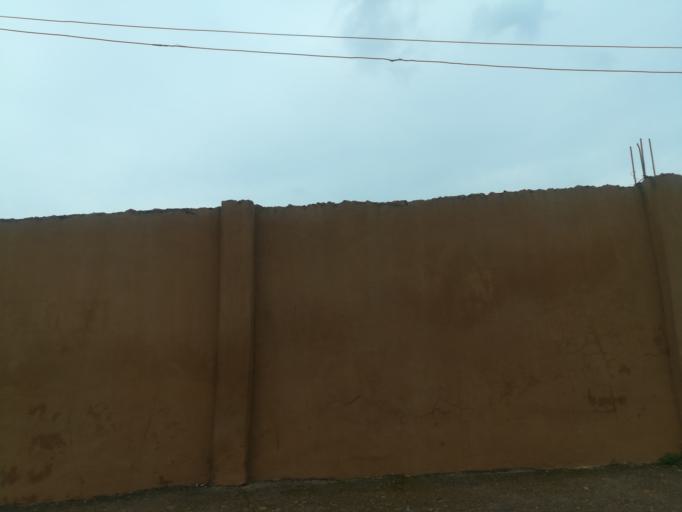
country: NG
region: Oyo
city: Ibadan
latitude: 7.3774
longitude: 3.9611
